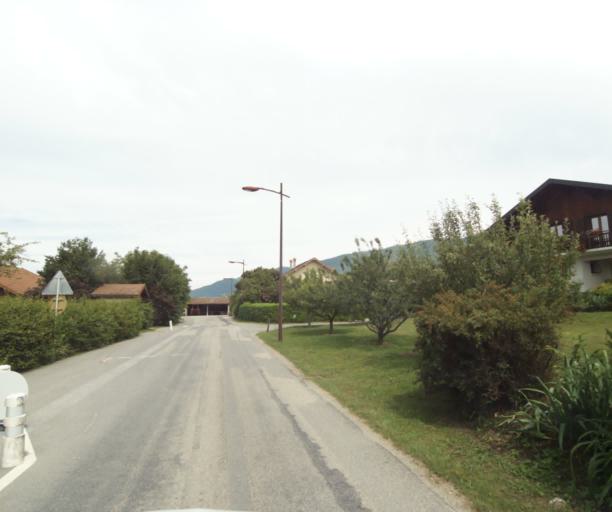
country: FR
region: Rhone-Alpes
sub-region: Departement de la Haute-Savoie
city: Bons-en-Chablais
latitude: 46.2744
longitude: 6.4105
